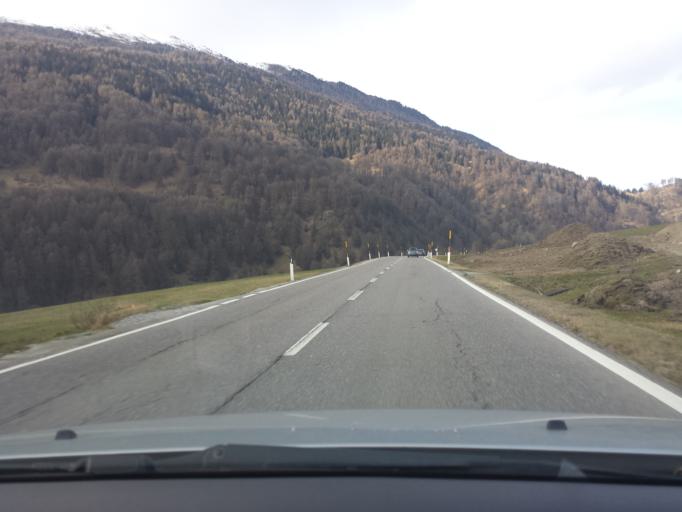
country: IT
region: Trentino-Alto Adige
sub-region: Bolzano
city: Malles Venosta
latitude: 46.7194
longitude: 10.5351
